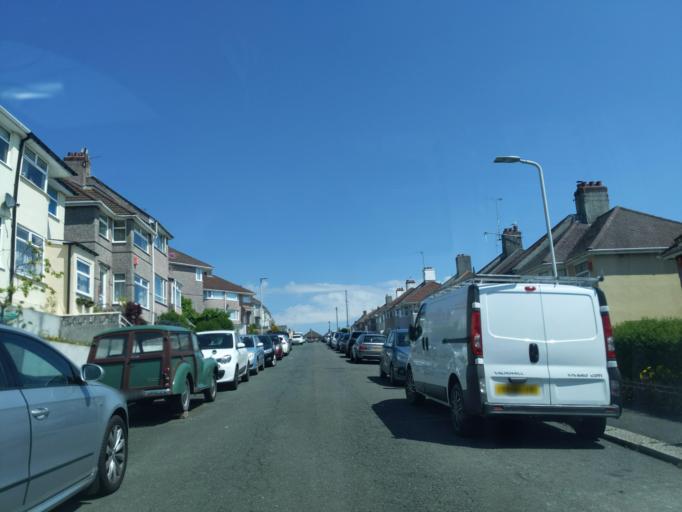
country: GB
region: England
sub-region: Cornwall
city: Torpoint
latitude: 50.3997
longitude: -4.1781
